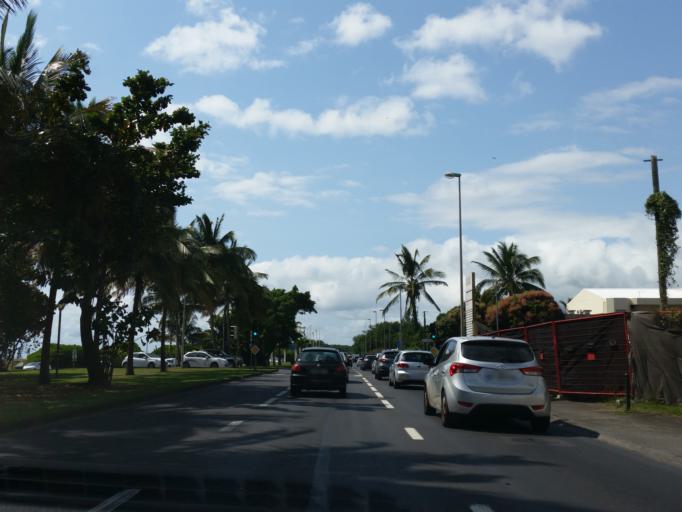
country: RE
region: Reunion
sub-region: Reunion
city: Saint-Denis
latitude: -20.8863
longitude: 55.4817
